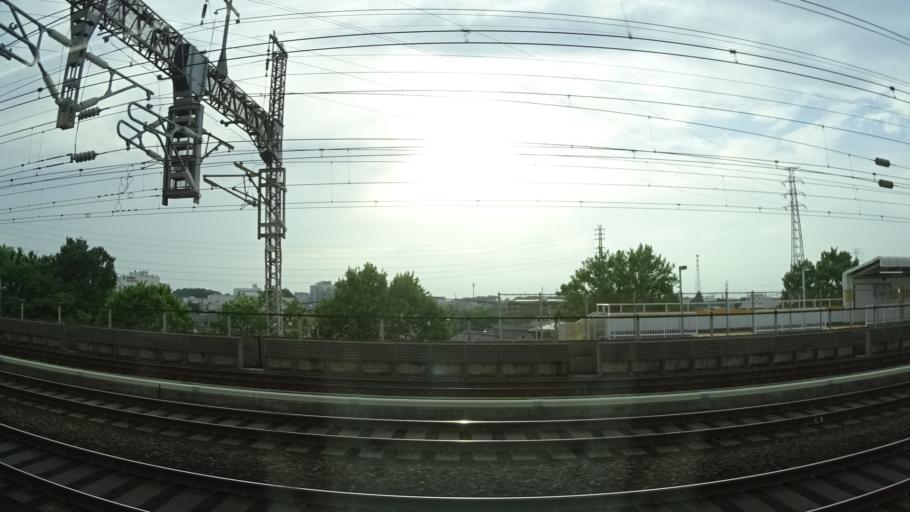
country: JP
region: Saitama
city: Ageoshimo
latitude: 35.9642
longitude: 139.6224
